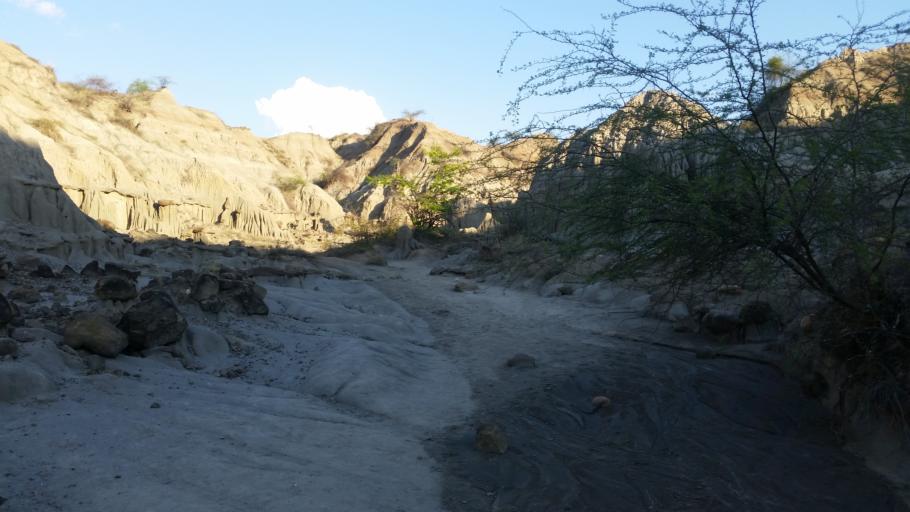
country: CO
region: Huila
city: Villavieja
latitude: 3.2384
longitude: -75.1190
